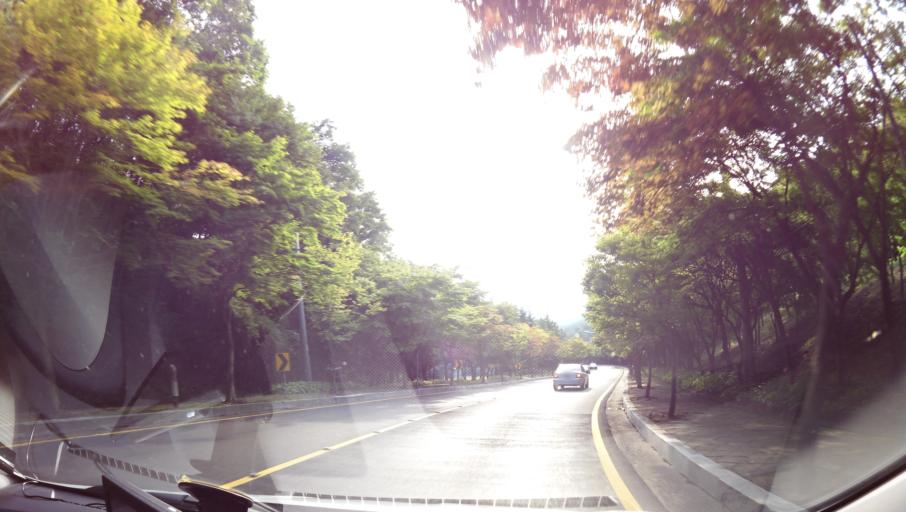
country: KR
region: Daegu
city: Daegu
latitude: 35.9850
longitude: 128.6572
